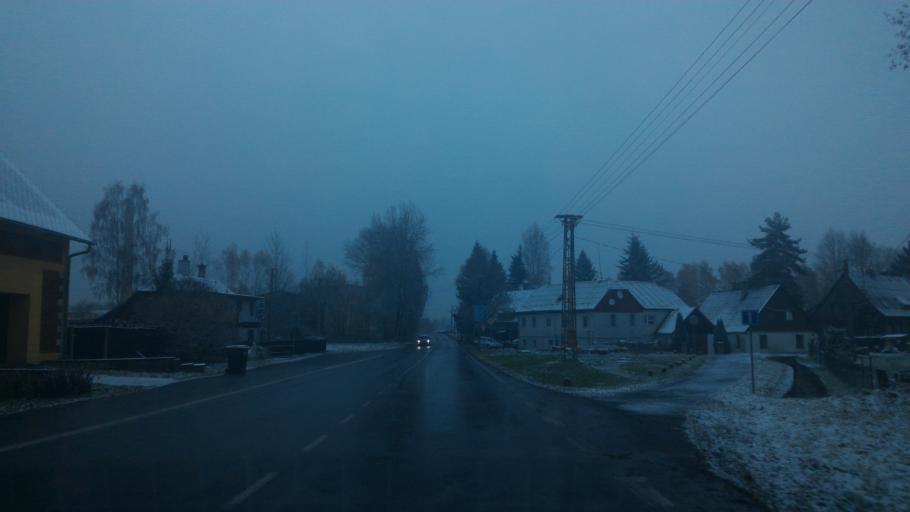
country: CZ
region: Ustecky
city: Jirikov
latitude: 50.9791
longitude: 14.5660
